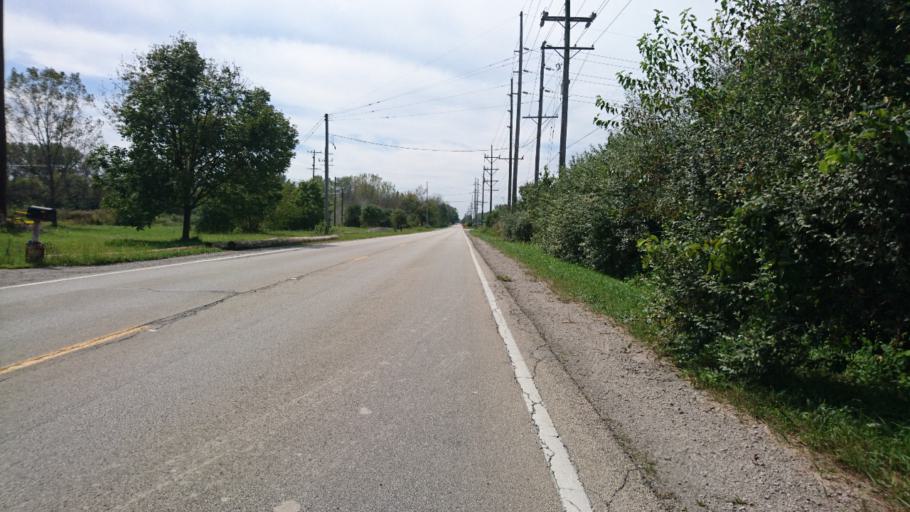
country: US
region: Illinois
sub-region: Will County
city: Lakewood Shores
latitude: 41.2916
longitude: -88.1769
